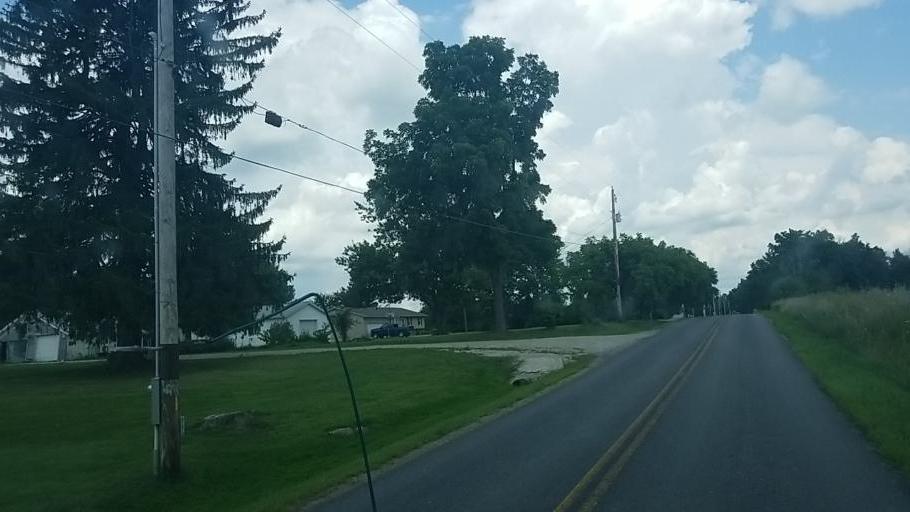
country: US
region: Ohio
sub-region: Medina County
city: Lodi
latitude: 41.0811
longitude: -82.0759
